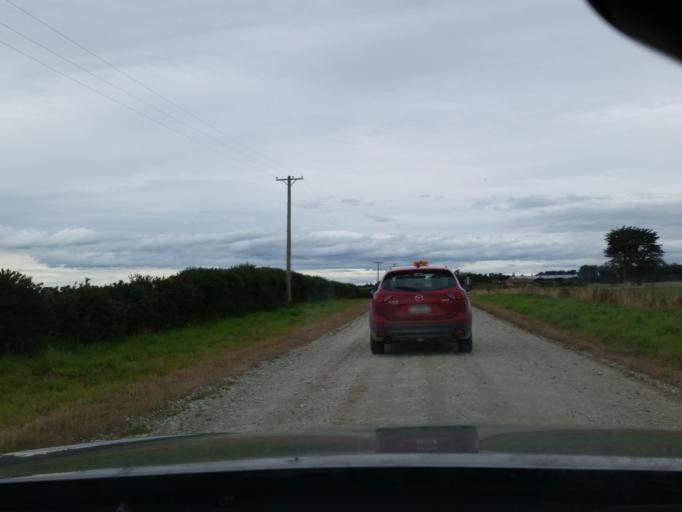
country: NZ
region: Southland
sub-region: Invercargill City
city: Invercargill
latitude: -46.3942
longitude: 168.5525
